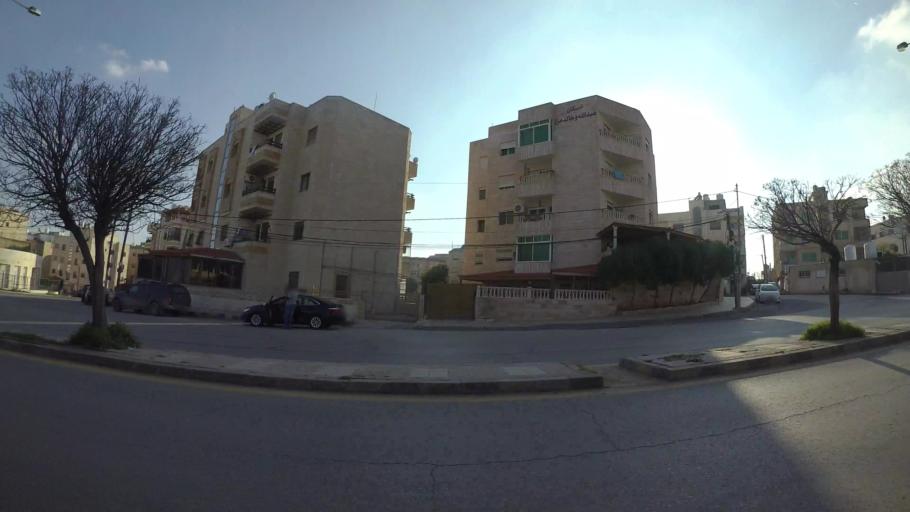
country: JO
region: Amman
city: Amman
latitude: 31.9824
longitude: 35.9373
